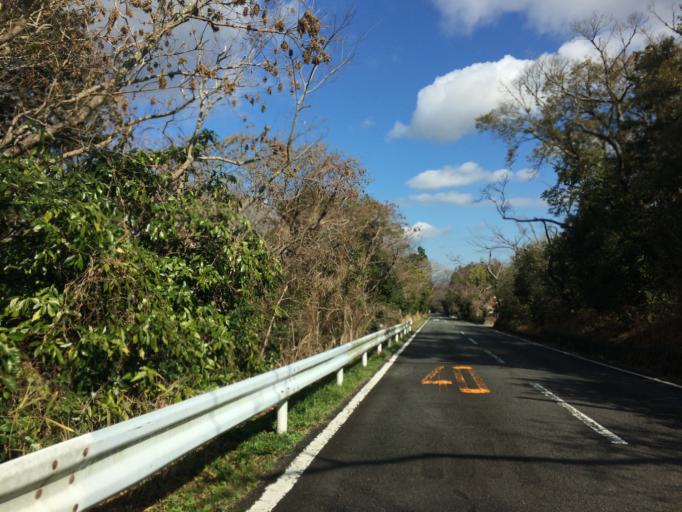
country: JP
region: Shizuoka
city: Shizuoka-shi
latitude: 34.9688
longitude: 138.4481
